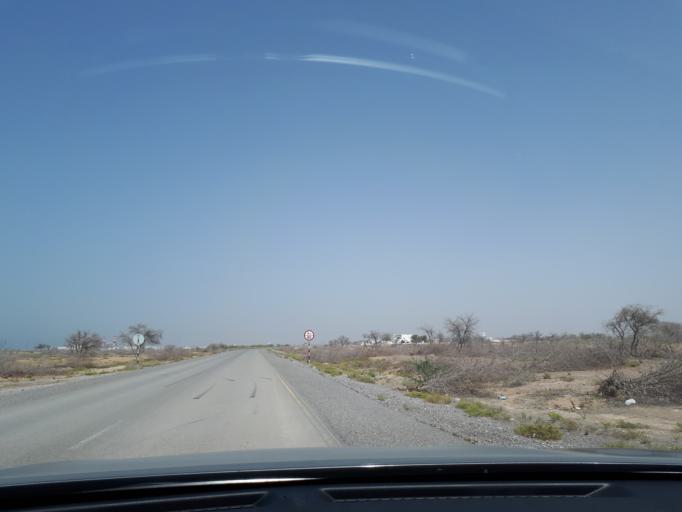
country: OM
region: Al Batinah
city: Barka'
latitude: 23.7022
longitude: 57.9555
